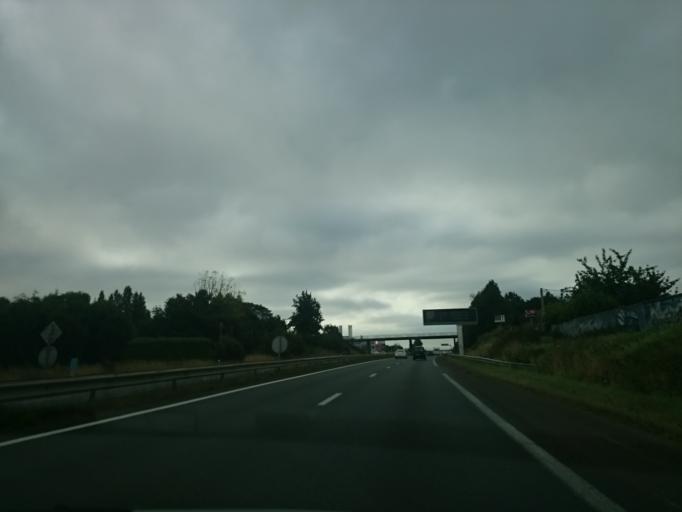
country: FR
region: Brittany
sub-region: Departement des Cotes-d'Armor
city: Plerin
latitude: 48.5389
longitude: -2.7625
